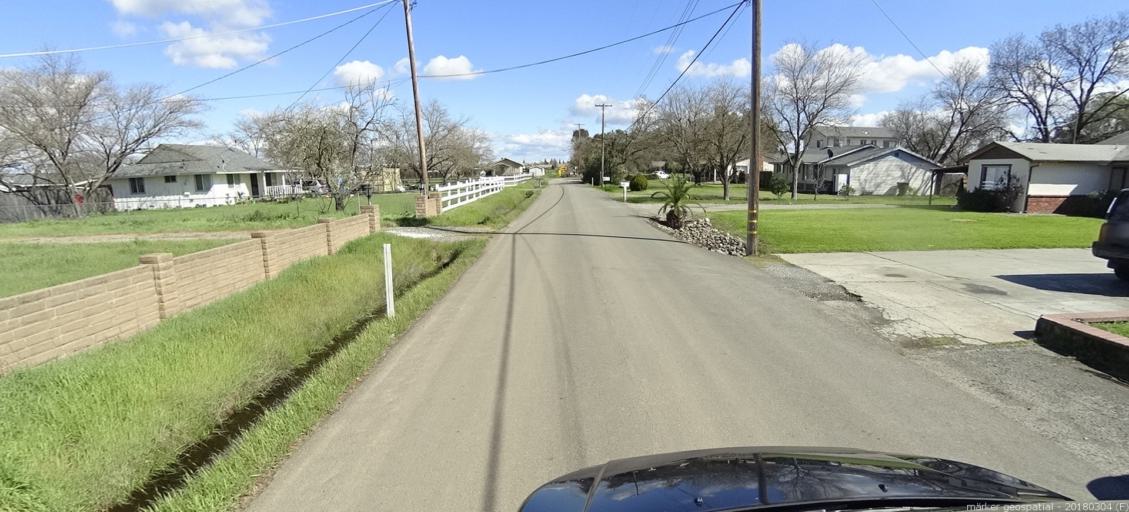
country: US
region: California
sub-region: Sacramento County
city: Vineyard
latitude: 38.4726
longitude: -121.3315
